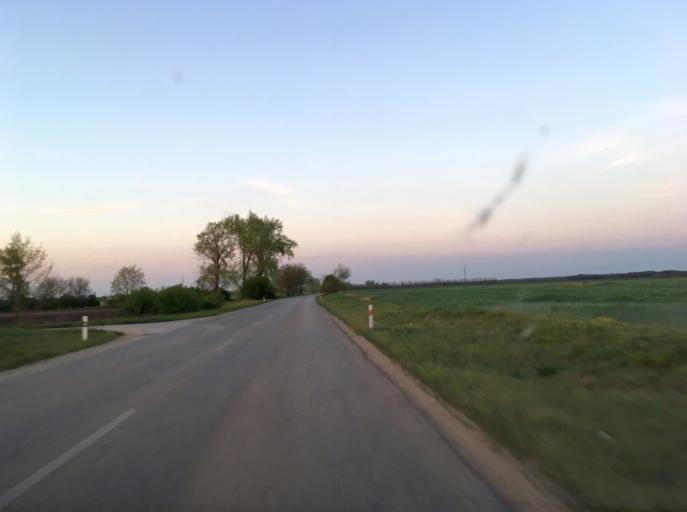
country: SK
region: Nitriansky
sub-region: Okres Nove Zamky
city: Nove Zamky
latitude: 47.9419
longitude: 18.1300
